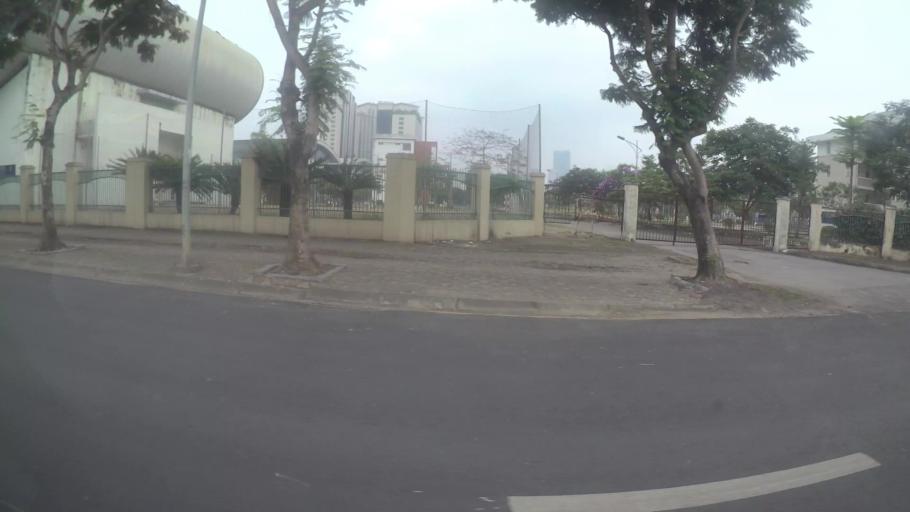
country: VN
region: Ha Noi
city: Cau Dien
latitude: 21.0278
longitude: 105.7637
